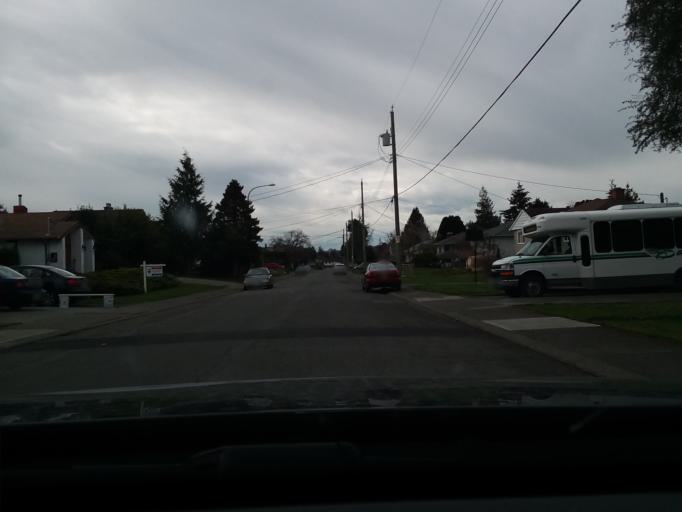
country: CA
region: British Columbia
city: Oak Bay
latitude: 48.4479
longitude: -123.3295
